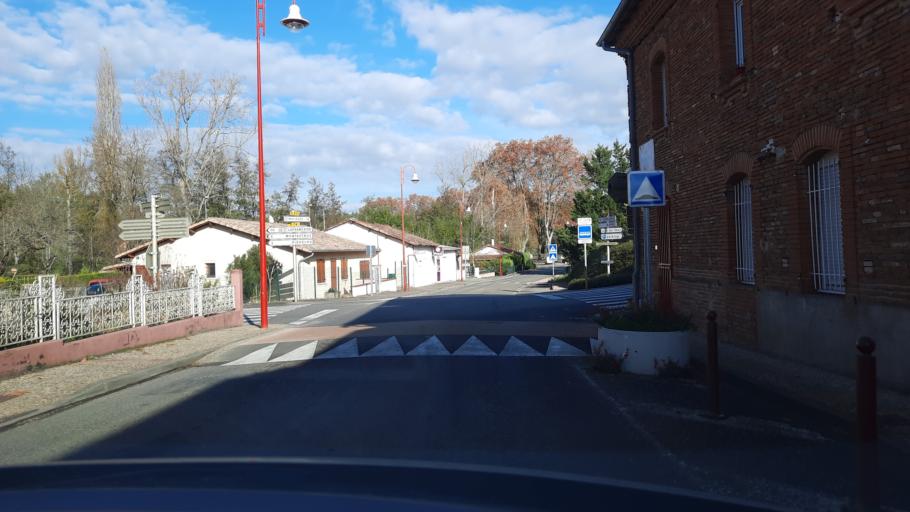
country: FR
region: Midi-Pyrenees
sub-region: Departement du Tarn-et-Garonne
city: Montauban
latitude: 44.0914
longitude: 1.3484
